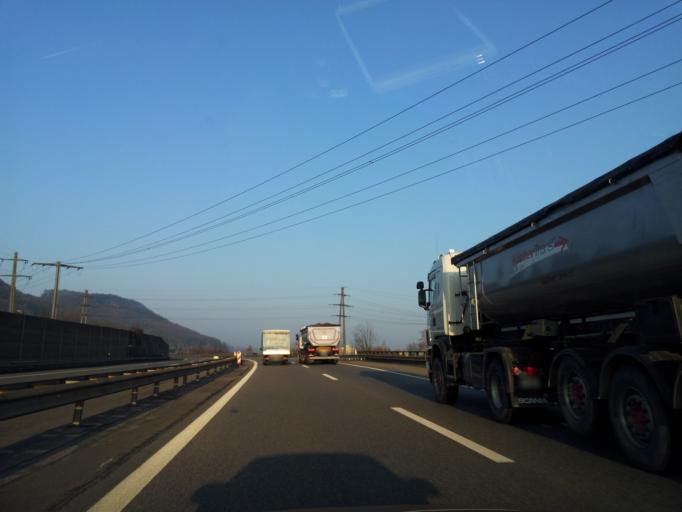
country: CH
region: Aargau
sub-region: Bezirk Rheinfelden
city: Stein
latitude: 47.5413
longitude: 7.9652
